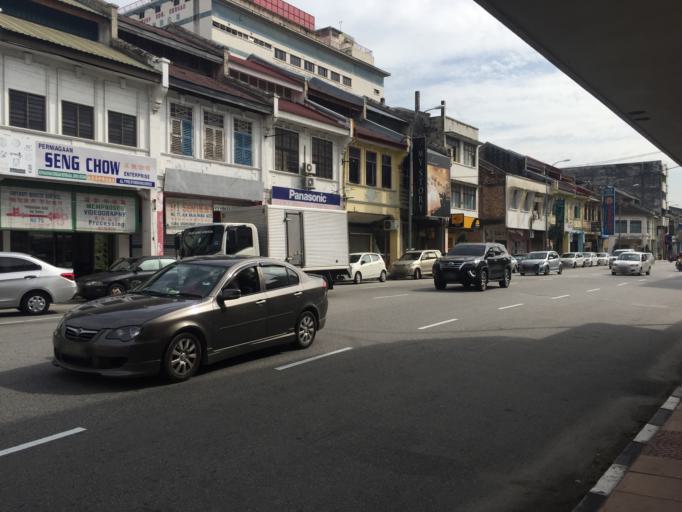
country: MY
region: Perak
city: Ipoh
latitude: 4.5983
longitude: 101.0845
